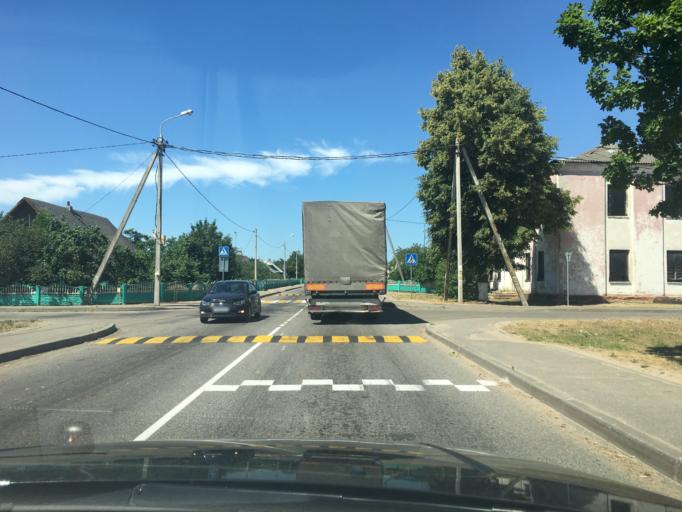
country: BY
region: Grodnenskaya
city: Iwye
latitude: 54.0330
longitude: 25.9254
